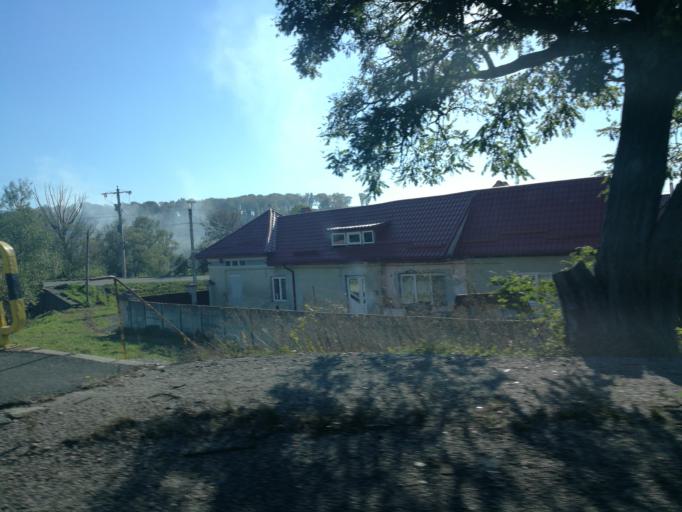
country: RO
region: Brasov
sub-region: Comuna Dumbravita
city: Dumbravita
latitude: 45.7677
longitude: 25.3633
